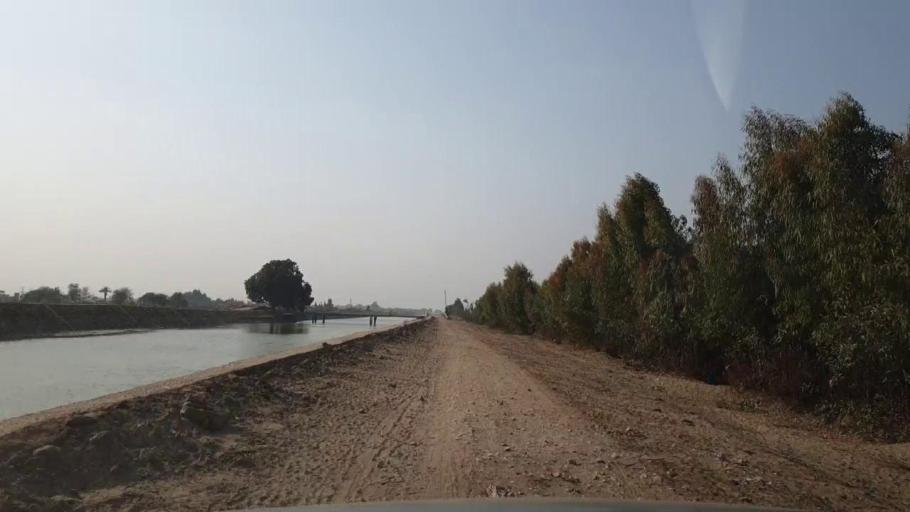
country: PK
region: Sindh
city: Matiari
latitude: 25.6410
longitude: 68.5804
